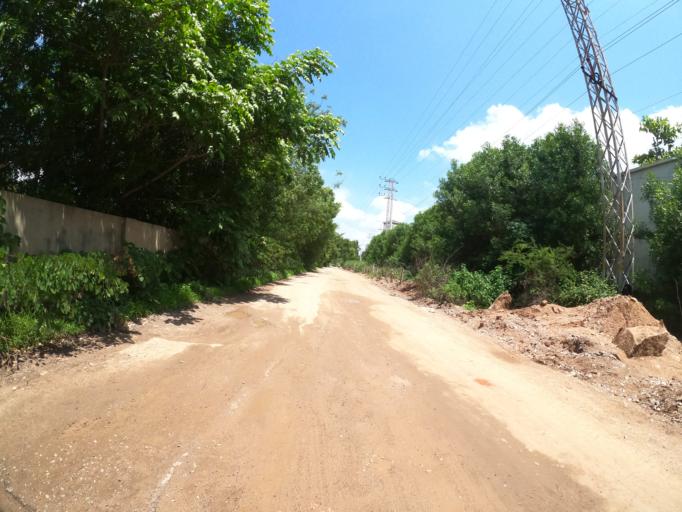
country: IN
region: Telangana
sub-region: Medak
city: Serilingampalle
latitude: 17.3742
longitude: 78.3229
